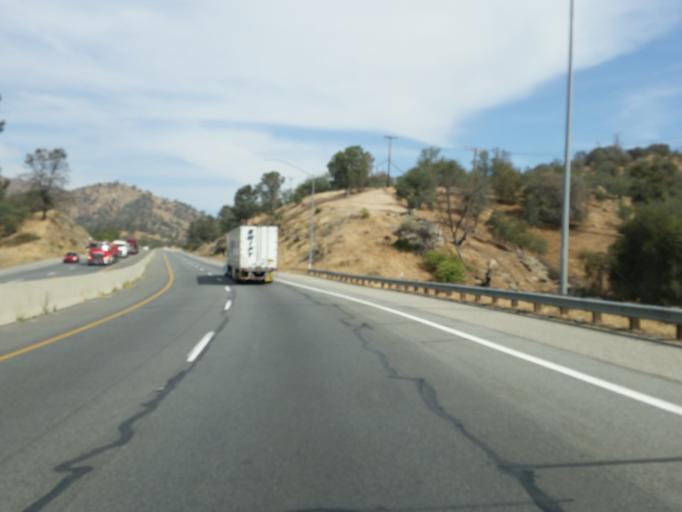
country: US
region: California
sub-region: Kern County
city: Bear Valley Springs
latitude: 35.2335
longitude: -118.5746
